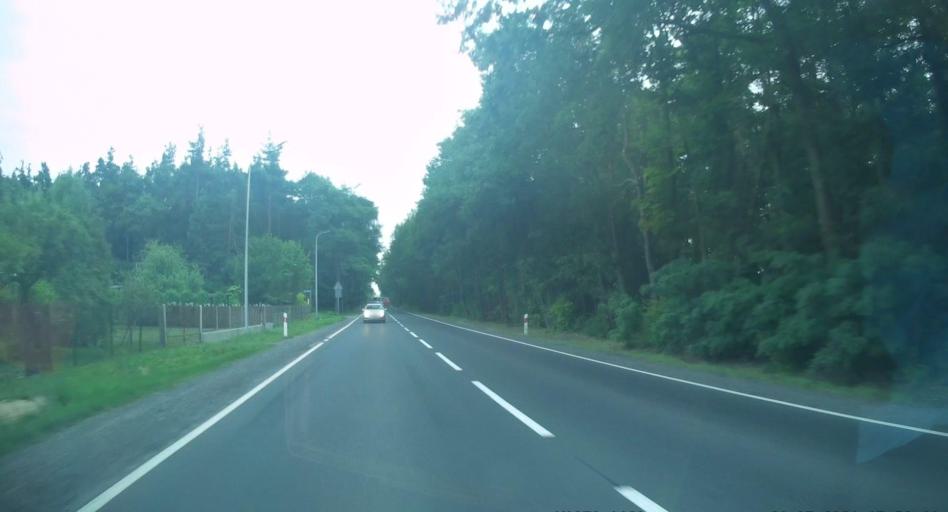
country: PL
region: Lodz Voivodeship
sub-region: Powiat radomszczanski
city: Gomunice
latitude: 51.1664
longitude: 19.4928
